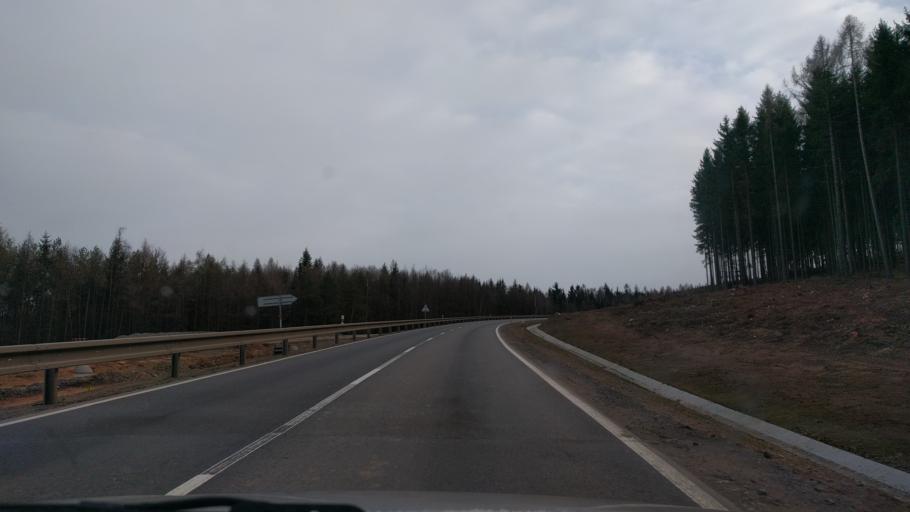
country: CZ
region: Central Bohemia
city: Milin
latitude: 49.6785
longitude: 14.0730
